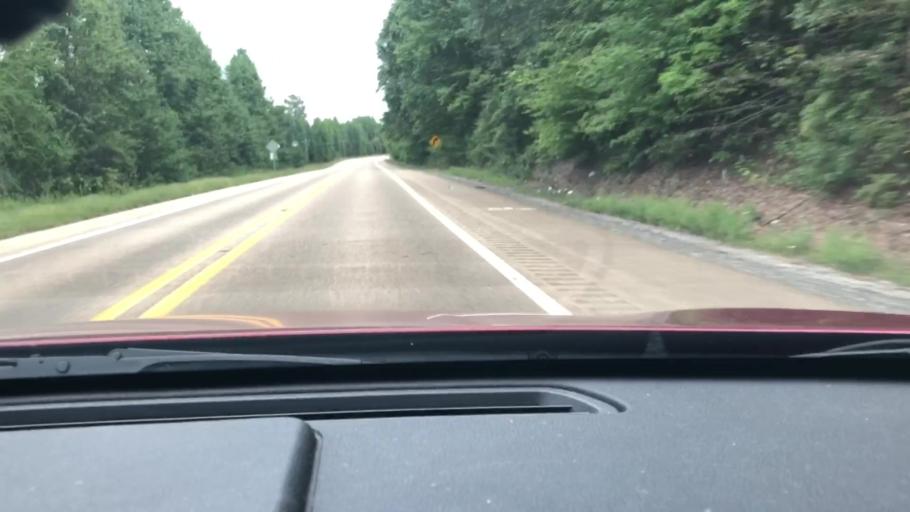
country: US
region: Arkansas
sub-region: Miller County
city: Texarkana
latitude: 33.4194
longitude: -93.8188
